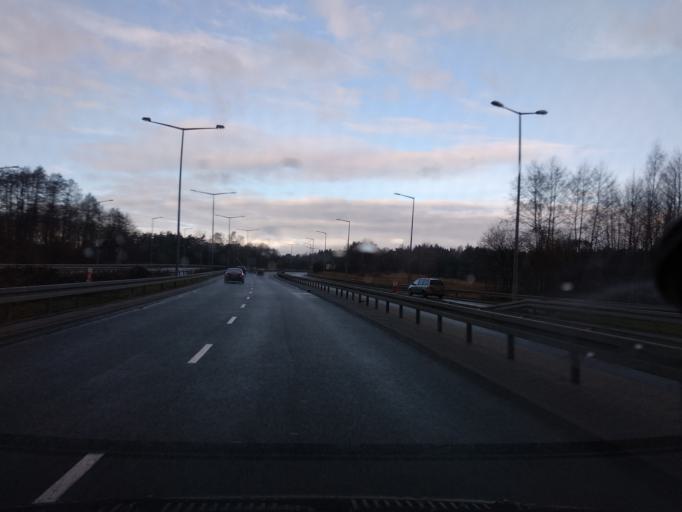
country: PL
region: Greater Poland Voivodeship
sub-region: Powiat koninski
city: Stare Miasto
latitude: 52.1886
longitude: 18.2281
